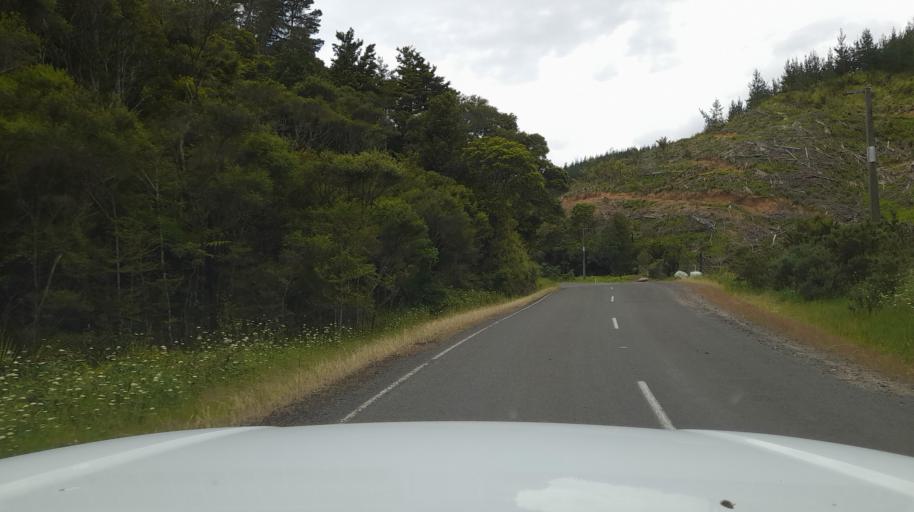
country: NZ
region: Northland
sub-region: Far North District
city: Kaitaia
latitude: -35.3658
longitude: 173.3902
